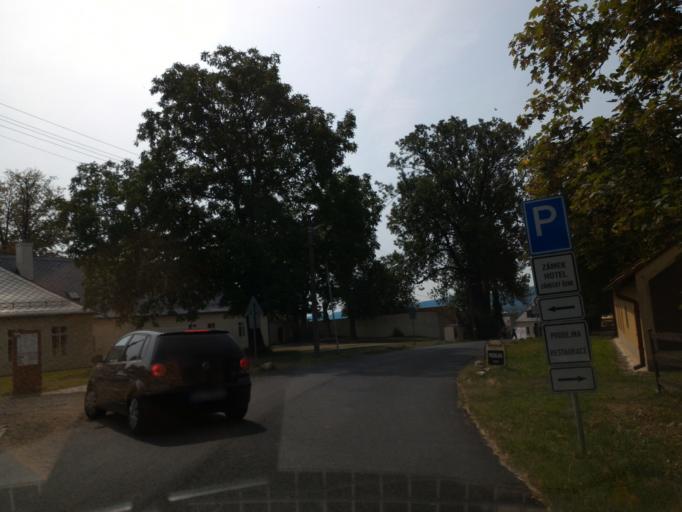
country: CZ
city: Prisovice
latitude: 50.5739
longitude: 15.0543
